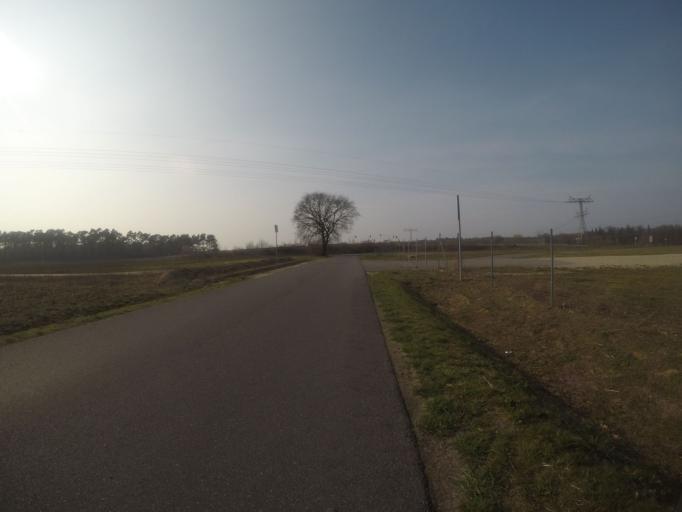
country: DE
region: Brandenburg
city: Rangsdorf
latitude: 52.3461
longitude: 13.4487
